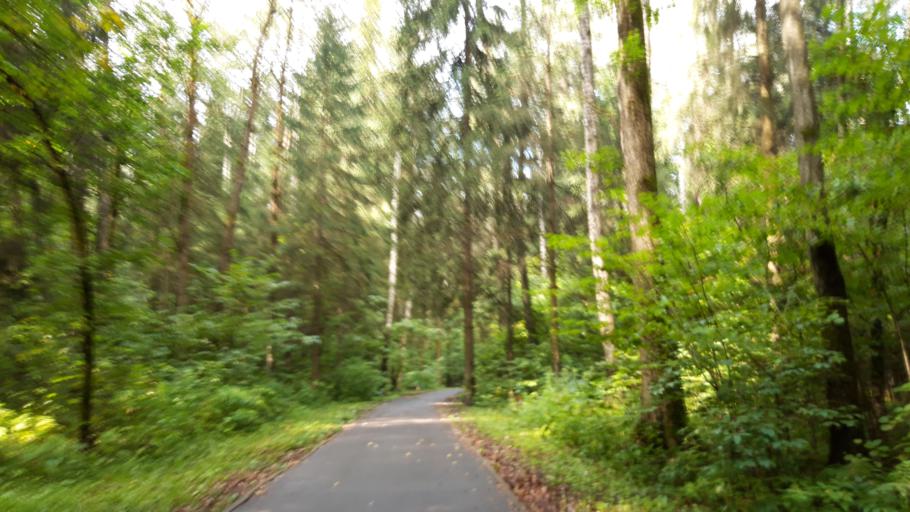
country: RU
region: Moscow
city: Zelenograd
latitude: 55.9850
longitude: 37.1999
